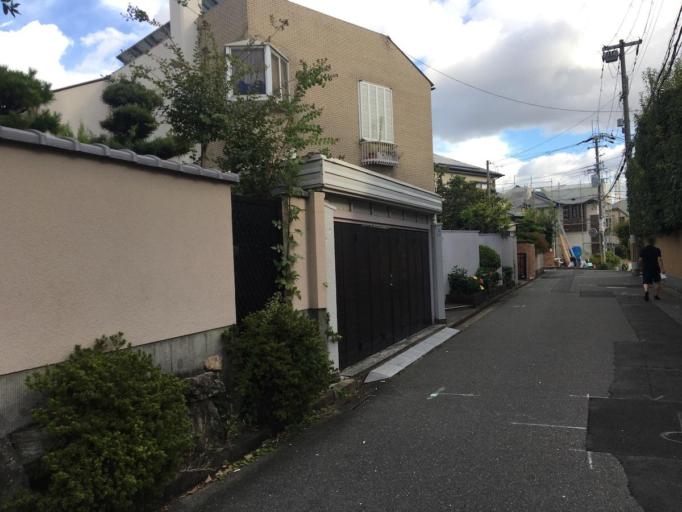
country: JP
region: Osaka
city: Suita
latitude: 34.7997
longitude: 135.5179
